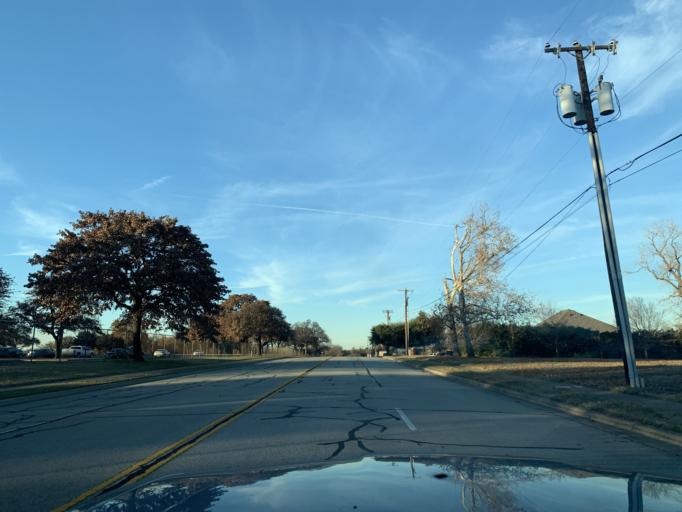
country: US
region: Texas
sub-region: Tarrant County
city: Bedford
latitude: 32.8392
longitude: -97.1373
